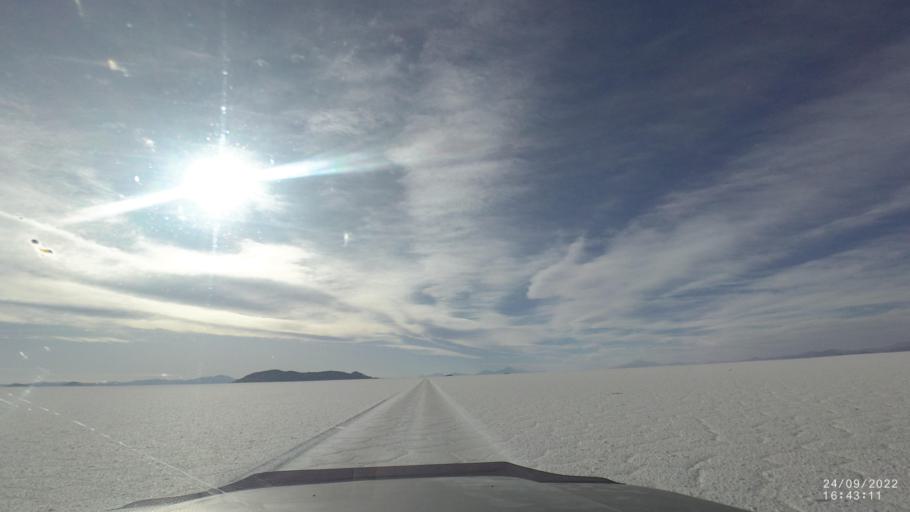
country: BO
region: Potosi
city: Colchani
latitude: -20.1680
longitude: -67.7430
